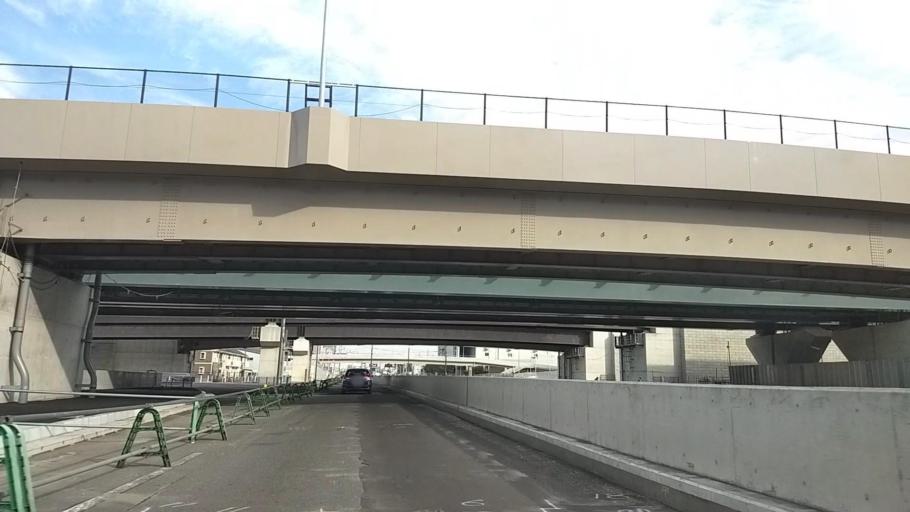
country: JP
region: Kanagawa
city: Atsugi
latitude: 35.4058
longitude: 139.3615
